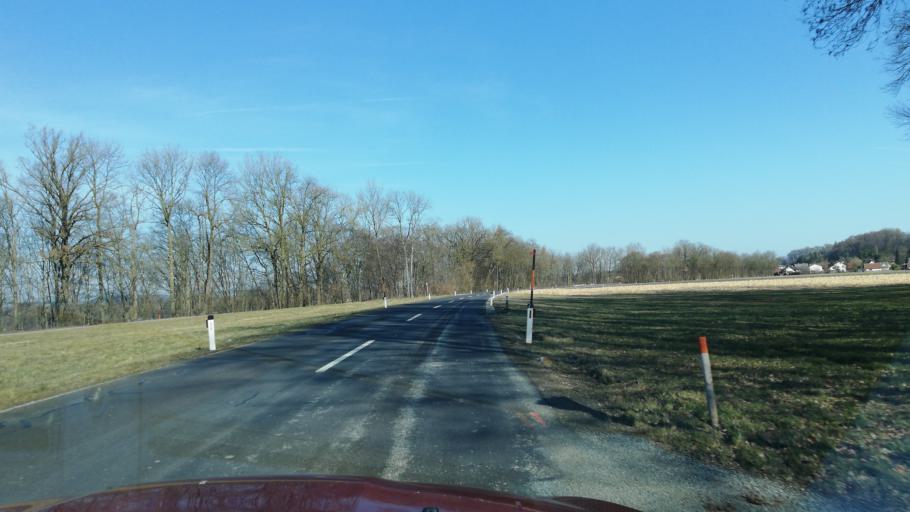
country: AT
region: Upper Austria
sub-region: Politischer Bezirk Vocklabruck
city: Rustorf
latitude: 48.0381
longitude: 13.7814
